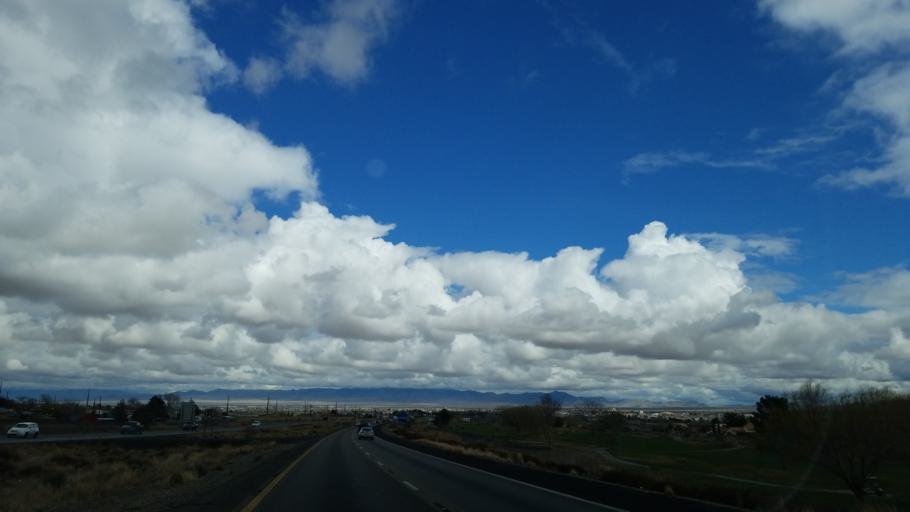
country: US
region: Arizona
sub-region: Mohave County
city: Kingman
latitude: 35.2100
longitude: -114.0552
